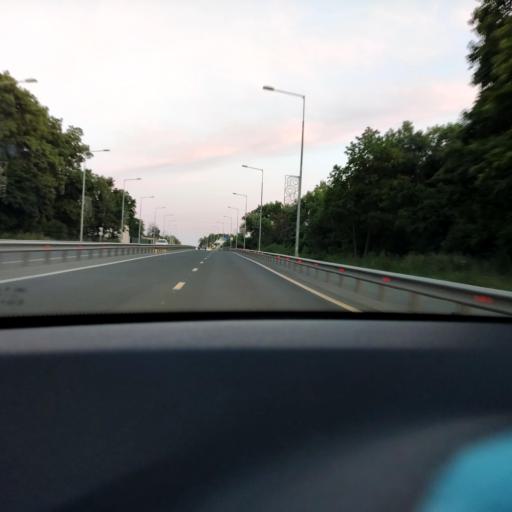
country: RU
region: Samara
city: Petra-Dubrava
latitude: 53.3007
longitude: 50.2424
